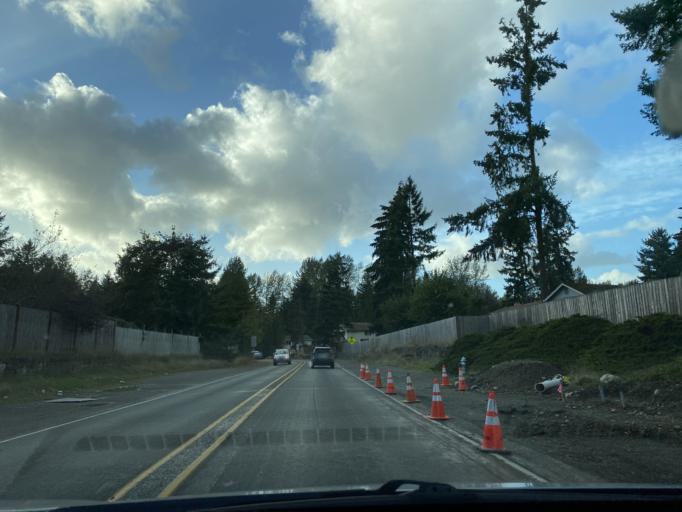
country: US
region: Washington
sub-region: Pierce County
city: South Hill
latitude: 47.1181
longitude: -122.2694
